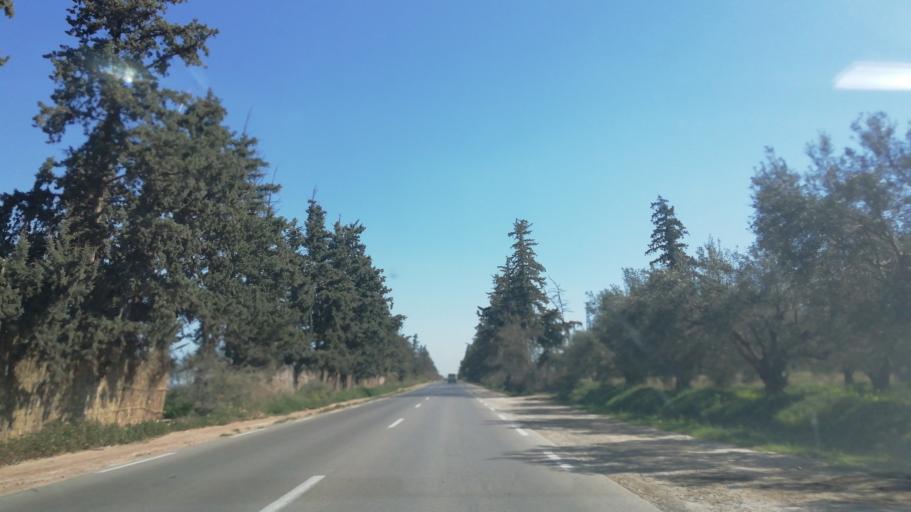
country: DZ
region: Mascara
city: Sig
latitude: 35.5674
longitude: -0.0659
